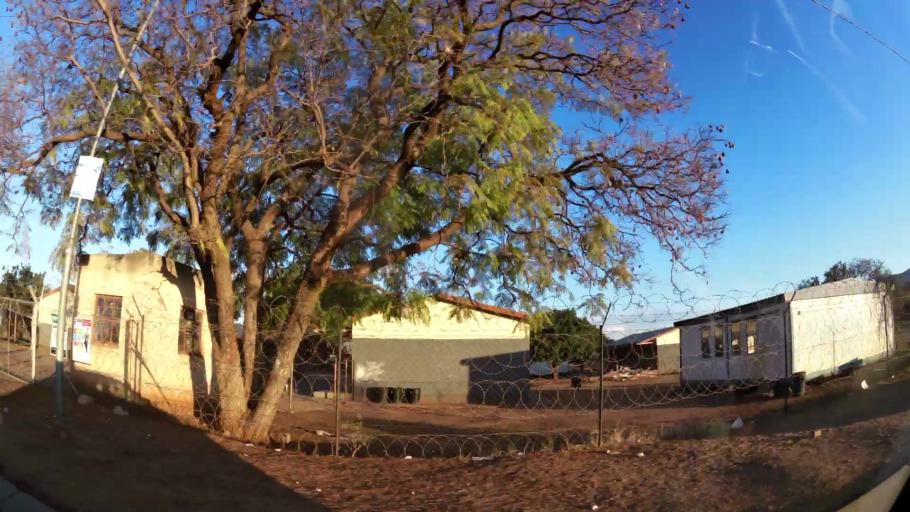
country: ZA
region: Limpopo
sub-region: Waterberg District Municipality
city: Mokopane
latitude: -24.1412
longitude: 28.9793
